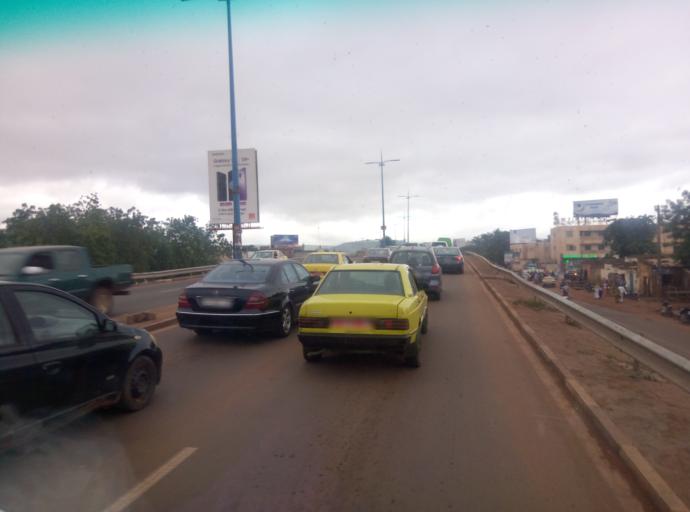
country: ML
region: Bamako
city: Bamako
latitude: 12.6130
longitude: -7.9987
